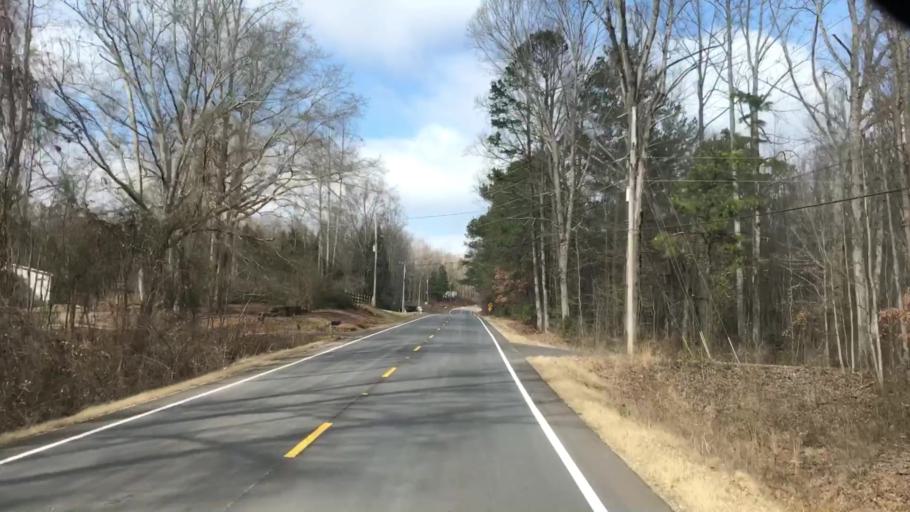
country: US
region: Georgia
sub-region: Jackson County
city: Braselton
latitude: 34.1387
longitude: -83.8358
